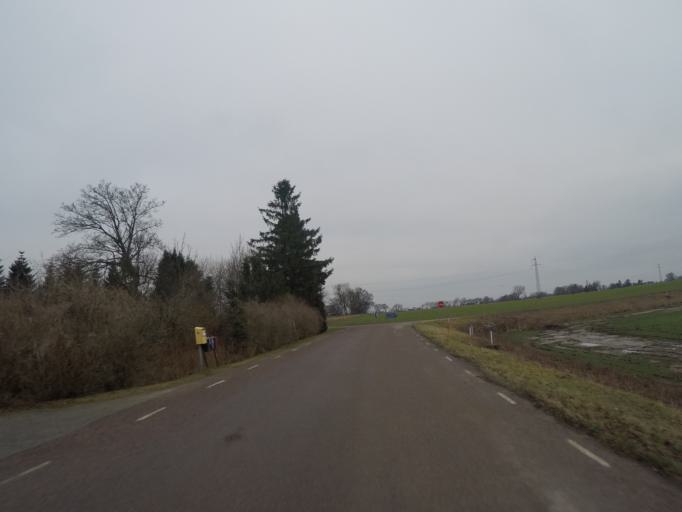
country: SE
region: Skane
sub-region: Hoors Kommun
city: Loberod
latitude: 55.7683
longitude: 13.4458
